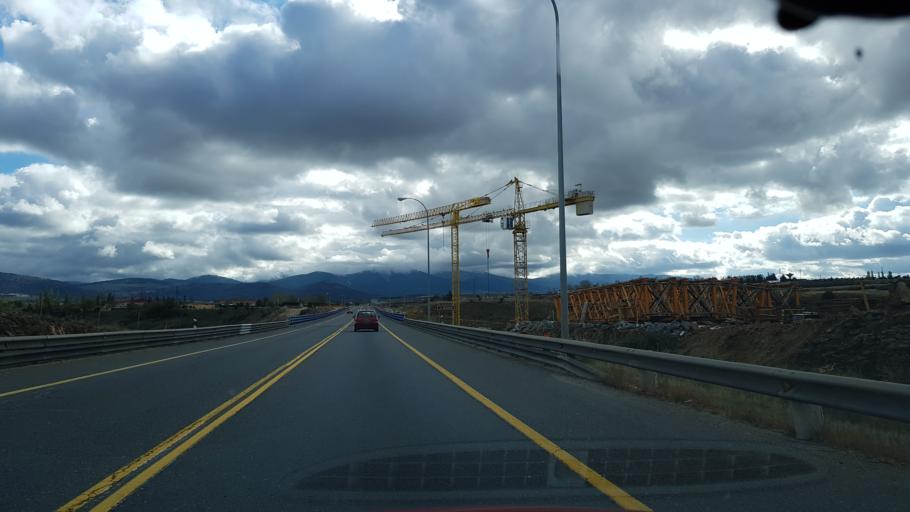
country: ES
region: Castille and Leon
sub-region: Provincia de Segovia
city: San Cristobal de Segovia
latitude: 40.9411
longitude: -4.0854
